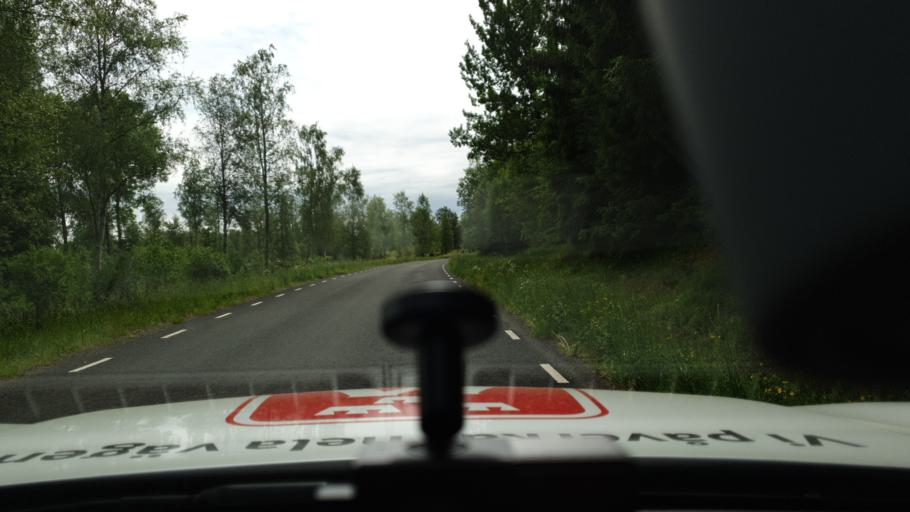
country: SE
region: Vaestra Goetaland
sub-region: Falkopings Kommun
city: Falkoeping
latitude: 58.0261
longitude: 13.6873
